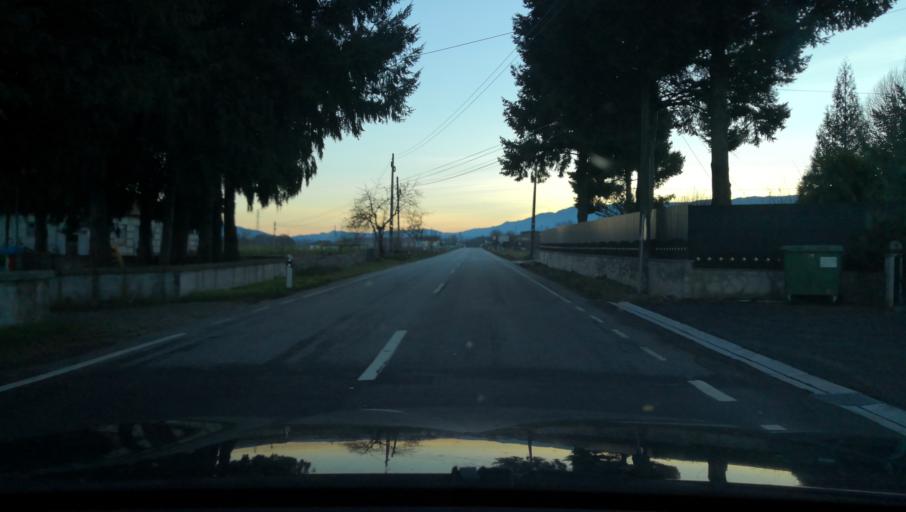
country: PT
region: Vila Real
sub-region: Vila Pouca de Aguiar
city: Vila Pouca de Aguiar
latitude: 41.4729
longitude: -7.6609
